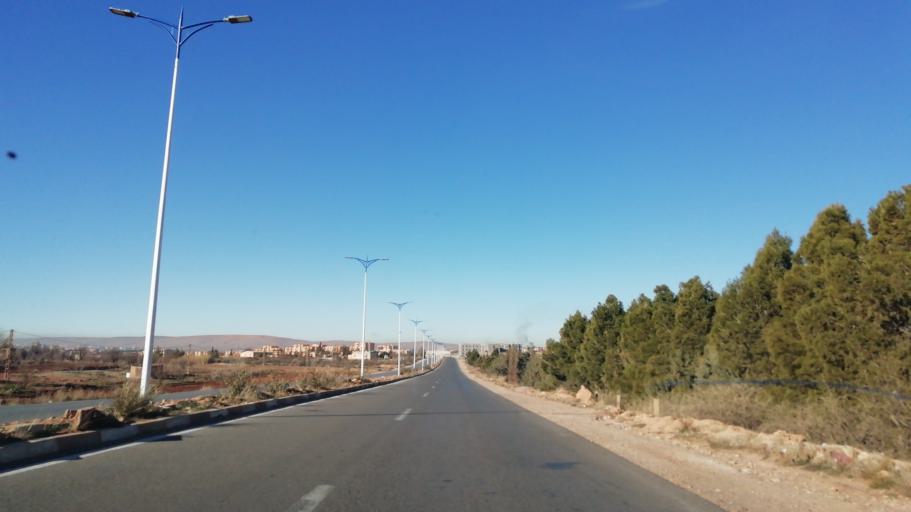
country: DZ
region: El Bayadh
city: El Bayadh
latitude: 33.6878
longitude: 1.0478
